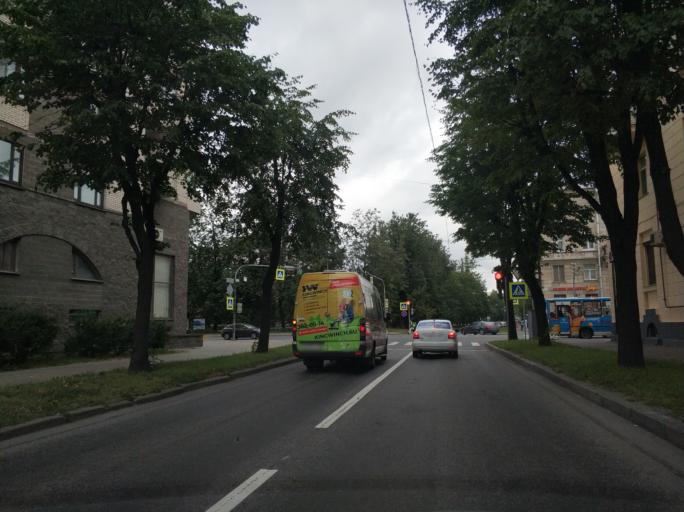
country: RU
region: St.-Petersburg
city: Novaya Derevnya
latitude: 59.9849
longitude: 30.2875
